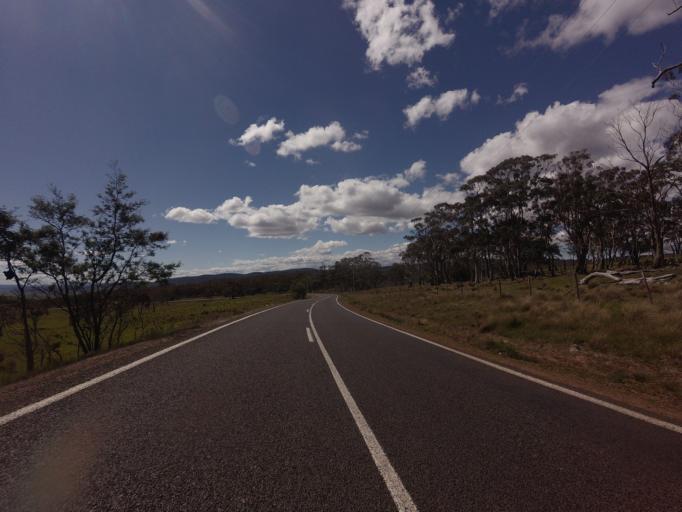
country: AU
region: Tasmania
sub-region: Northern Midlands
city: Evandale
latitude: -41.9446
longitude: 147.6043
